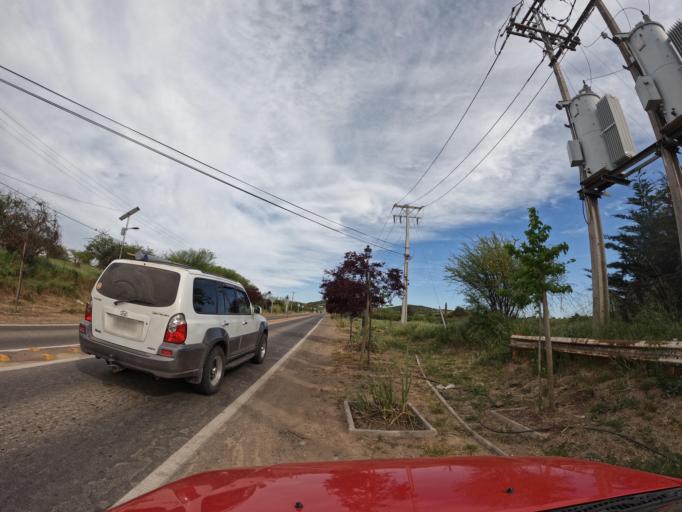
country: CL
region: Maule
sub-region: Provincia de Talca
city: Talca
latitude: -35.3994
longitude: -71.7974
